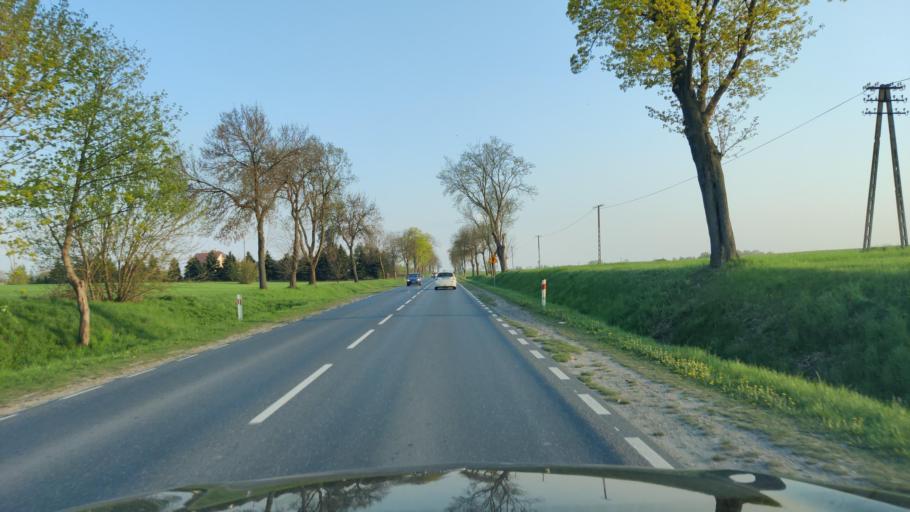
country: PL
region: Masovian Voivodeship
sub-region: Powiat pultuski
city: Pultusk
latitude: 52.6665
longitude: 21.0815
